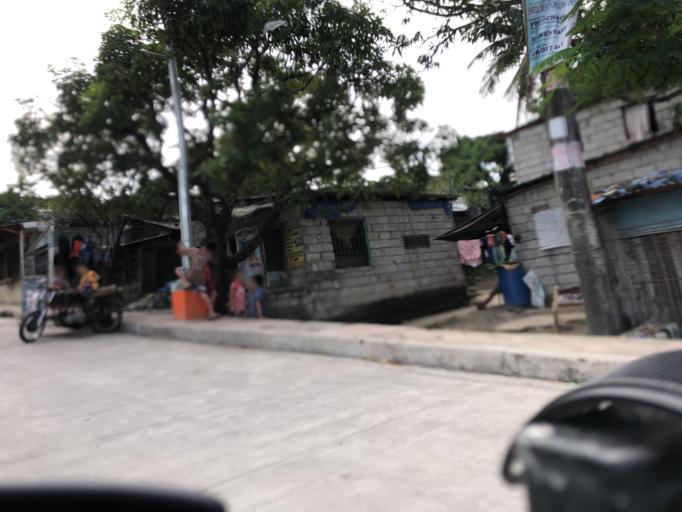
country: PH
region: Central Luzon
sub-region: Province of Bulacan
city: San Jose del Monte
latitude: 14.7486
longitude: 121.0573
